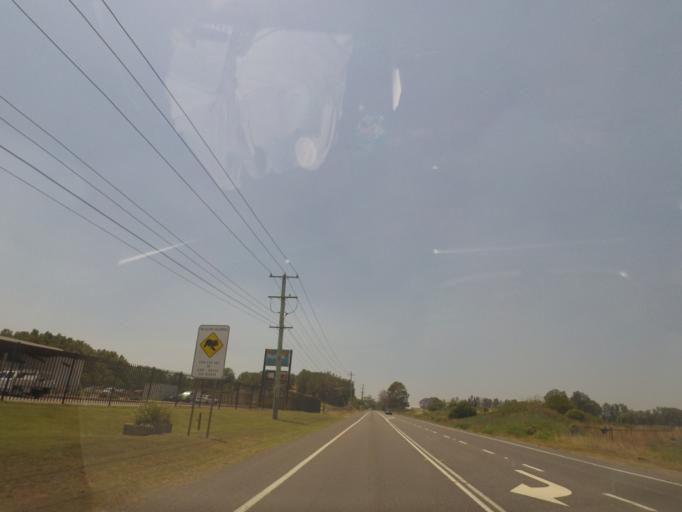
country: AU
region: New South Wales
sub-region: Port Stephens Shire
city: Medowie
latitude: -32.8070
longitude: 151.8673
